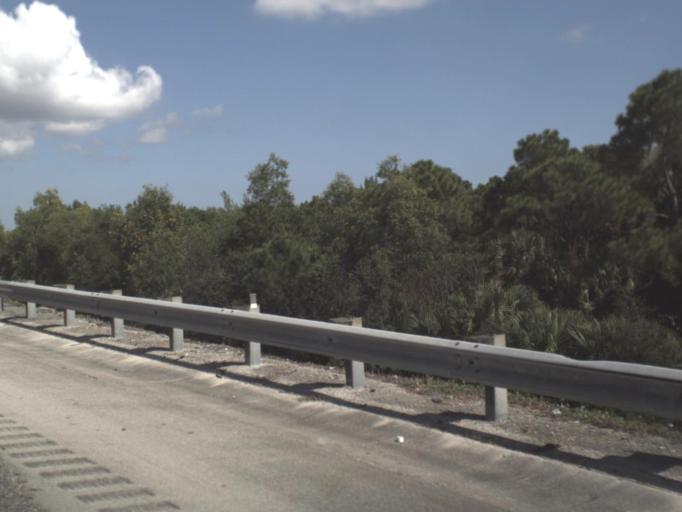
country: US
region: Florida
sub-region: Palm Beach County
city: Palm Beach Gardens
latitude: 26.7925
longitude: -80.1317
